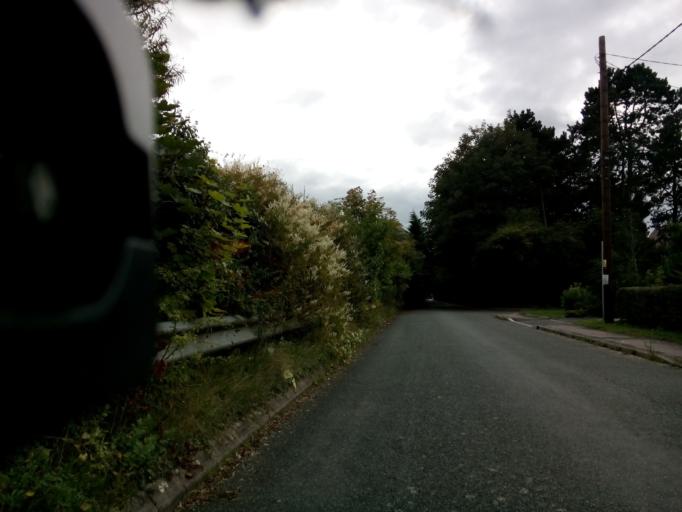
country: GB
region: England
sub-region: Suffolk
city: Capel Saint Mary
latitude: 52.0045
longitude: 1.0579
